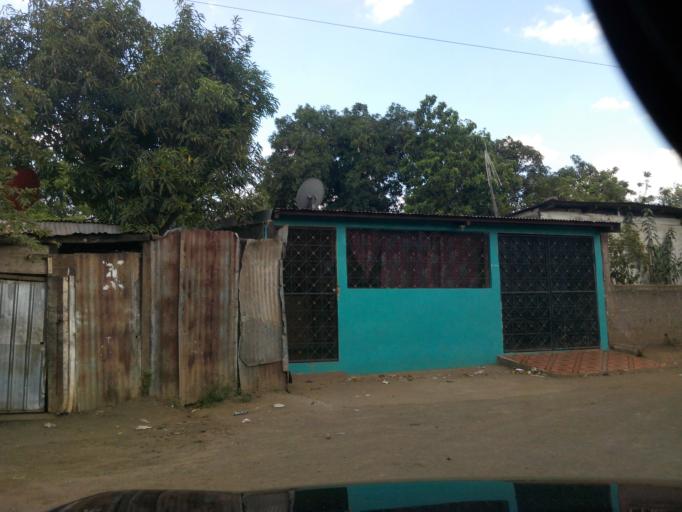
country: NI
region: Managua
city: Managua
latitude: 12.1345
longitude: -86.2635
